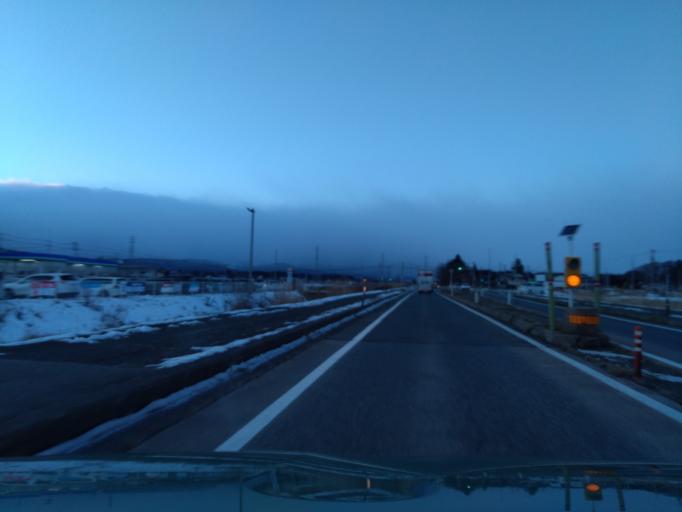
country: JP
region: Iwate
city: Shizukuishi
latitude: 39.6974
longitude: 140.9780
